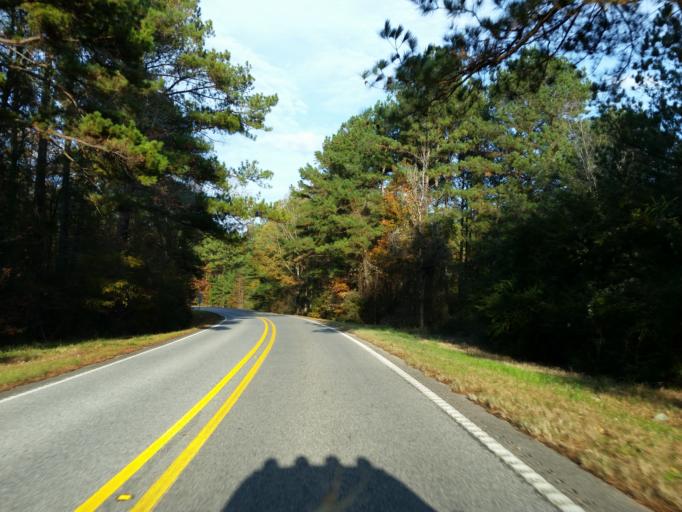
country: US
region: Mississippi
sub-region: Clarke County
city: Stonewall
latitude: 32.2003
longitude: -88.7993
